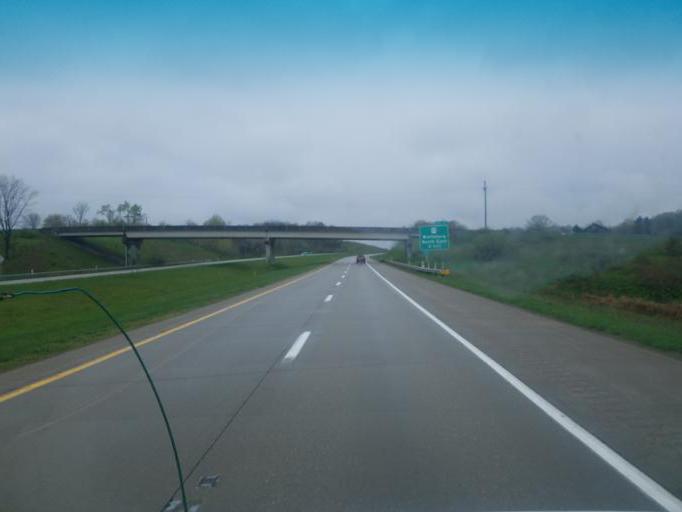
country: US
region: Pennsylvania
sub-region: Erie County
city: North East
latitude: 42.1265
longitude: -79.7817
